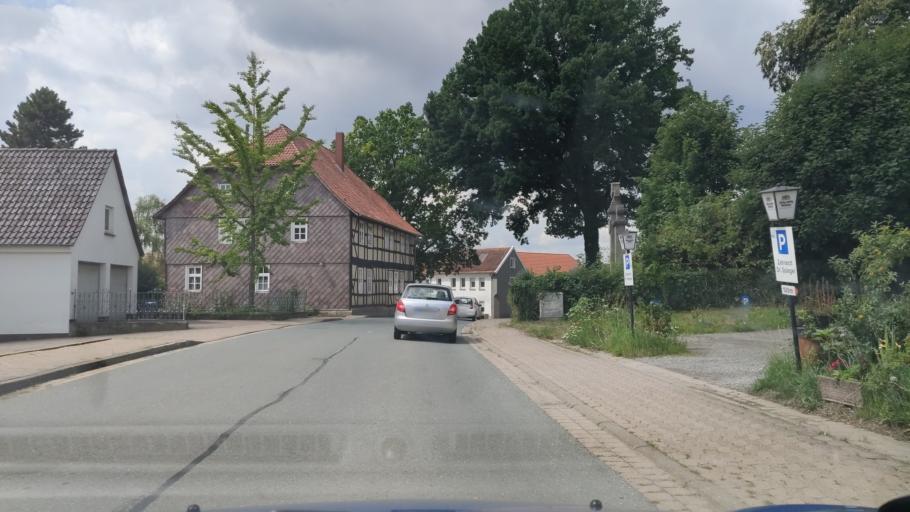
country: DE
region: Lower Saxony
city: Coppenbrugge
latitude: 52.0853
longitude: 9.5011
